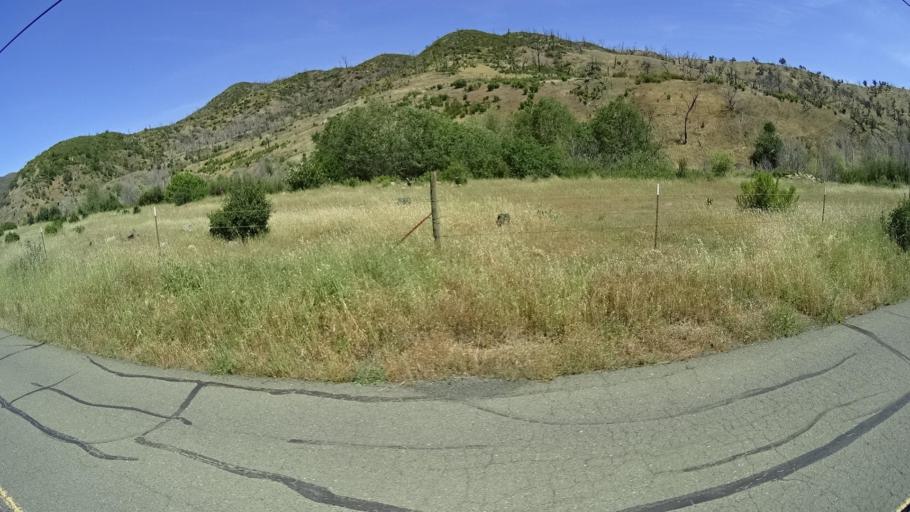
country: US
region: California
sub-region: Lake County
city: Middletown
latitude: 38.7780
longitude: -122.6345
